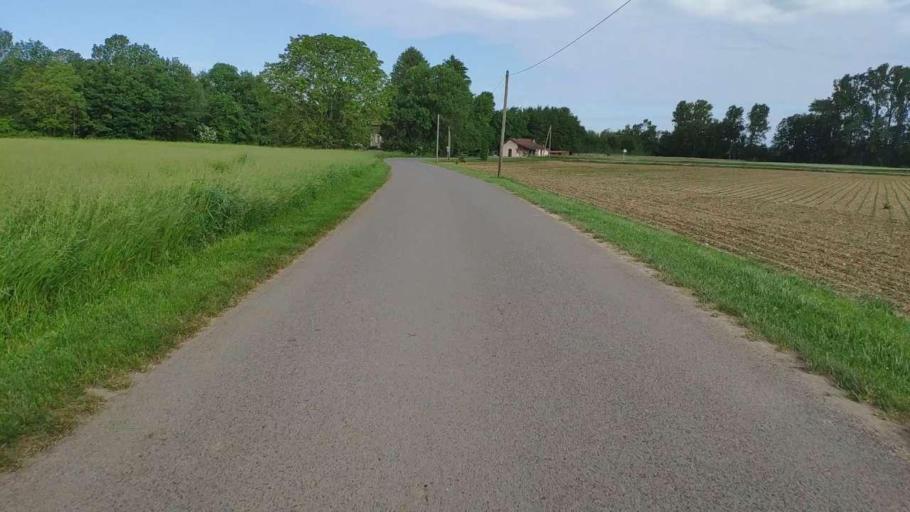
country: FR
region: Franche-Comte
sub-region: Departement du Jura
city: Bletterans
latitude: 46.7361
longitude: 5.4722
